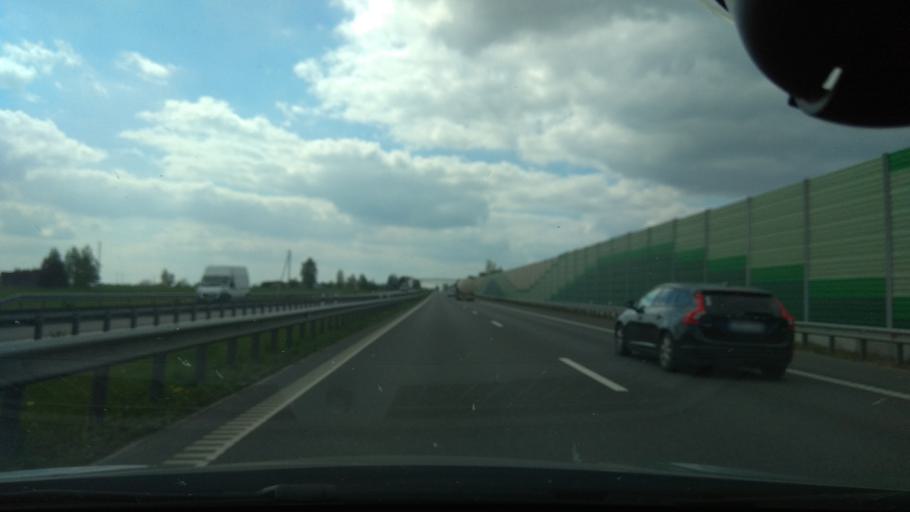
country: LT
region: Kauno apskritis
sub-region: Kauno rajonas
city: Mastaiciai
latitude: 54.7947
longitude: 23.8128
